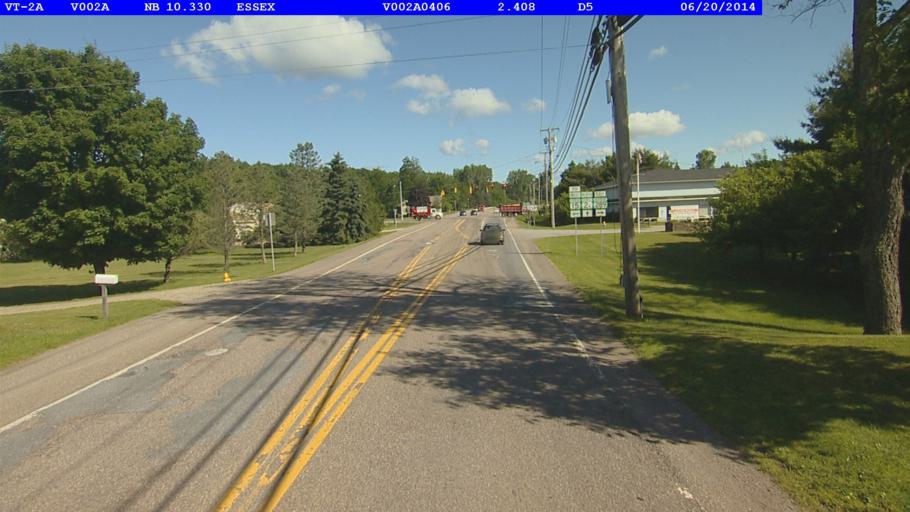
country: US
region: Vermont
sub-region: Chittenden County
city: Essex Junction
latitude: 44.5143
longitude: -73.1217
